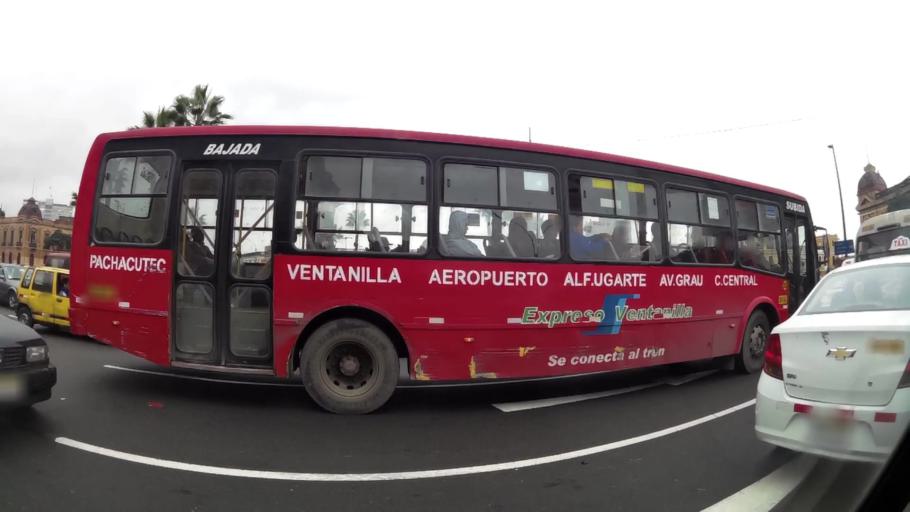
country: PE
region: Lima
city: Lima
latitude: -12.0600
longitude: -77.0420
